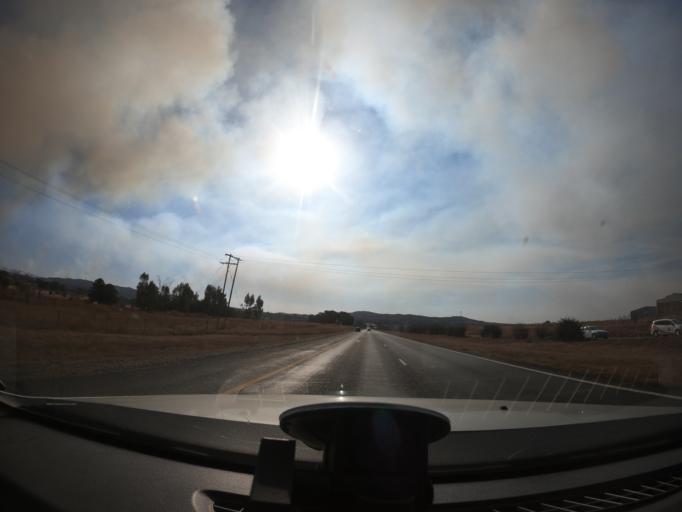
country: ZA
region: Gauteng
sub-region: Sedibeng District Municipality
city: Heidelberg
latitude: -26.5091
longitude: 28.3856
